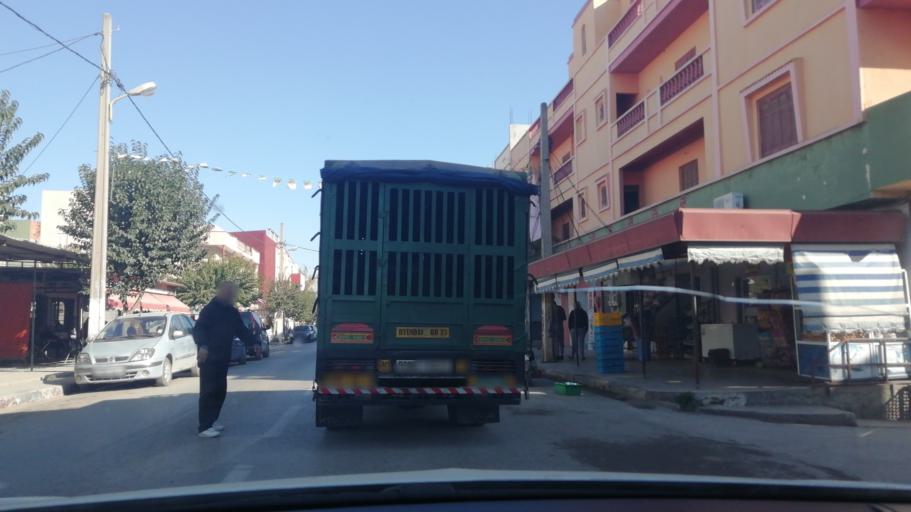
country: DZ
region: Tlemcen
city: Nedroma
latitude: 35.0433
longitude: -1.8864
